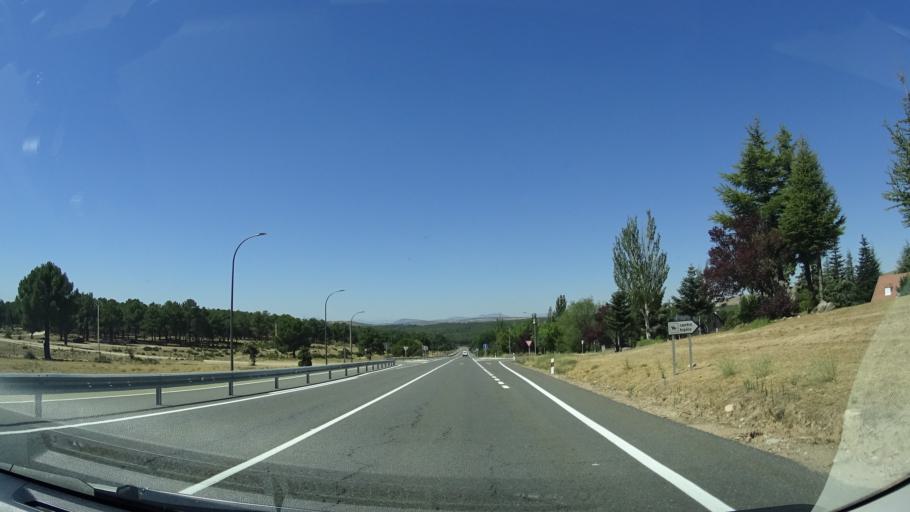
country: ES
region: Castille and Leon
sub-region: Provincia de Avila
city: Las Navas del Marques
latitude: 40.5974
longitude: -4.3458
